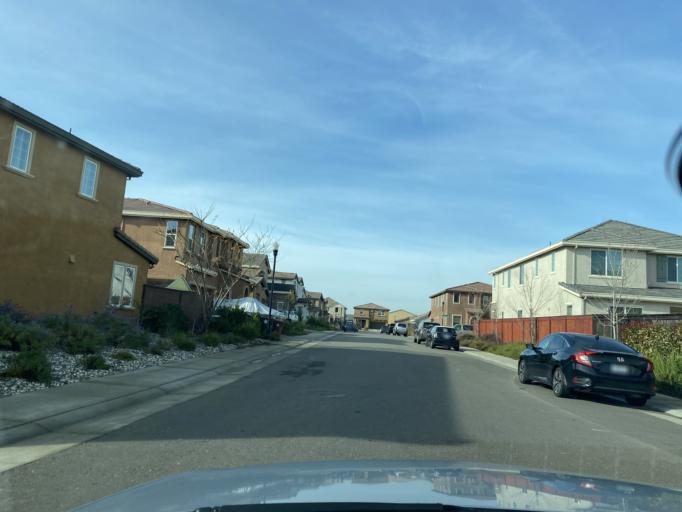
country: US
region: California
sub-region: Sacramento County
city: Elk Grove
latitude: 38.3983
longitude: -121.3924
